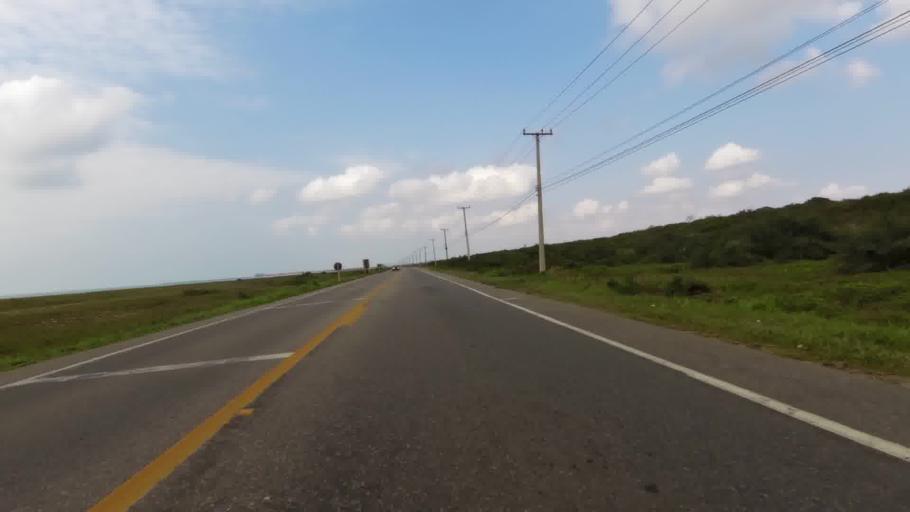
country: BR
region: Espirito Santo
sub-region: Itapemirim
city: Itapemirim
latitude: -20.9691
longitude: -40.8110
